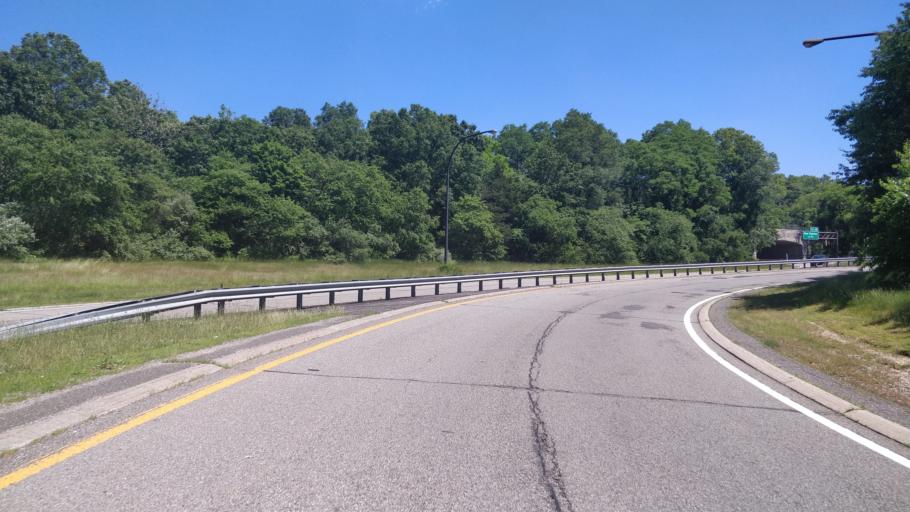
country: US
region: New York
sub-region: Suffolk County
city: Commack
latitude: 40.8195
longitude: -73.2885
